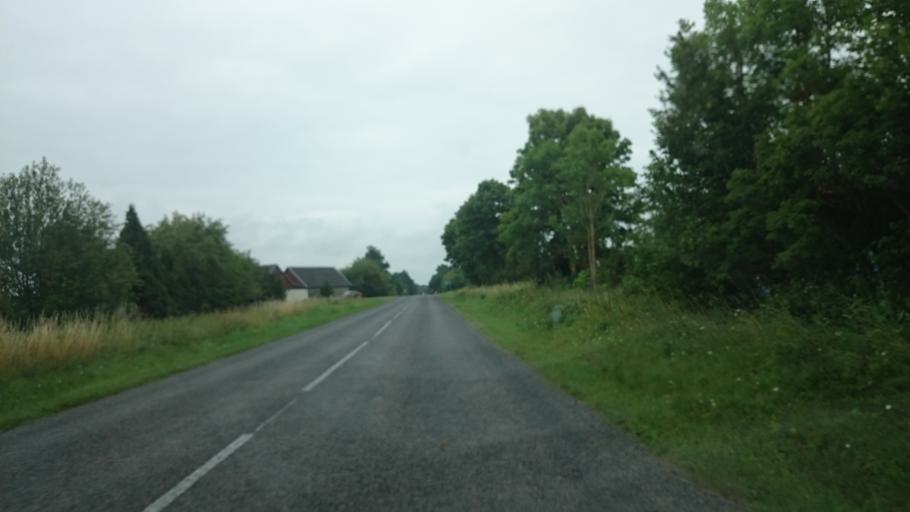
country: EE
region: Saare
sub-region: Orissaare vald
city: Orissaare
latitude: 58.5824
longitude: 23.0268
